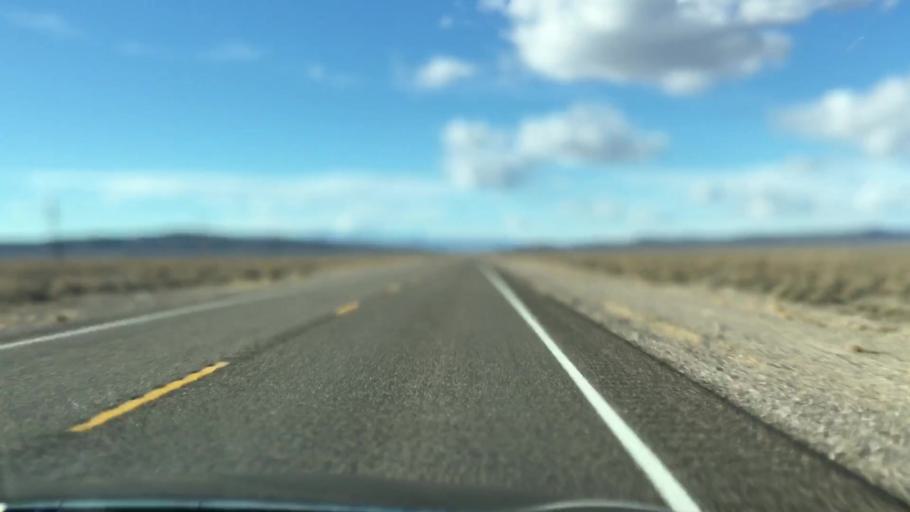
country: US
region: Nevada
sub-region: Nye County
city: Beatty
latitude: 37.1337
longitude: -116.8470
